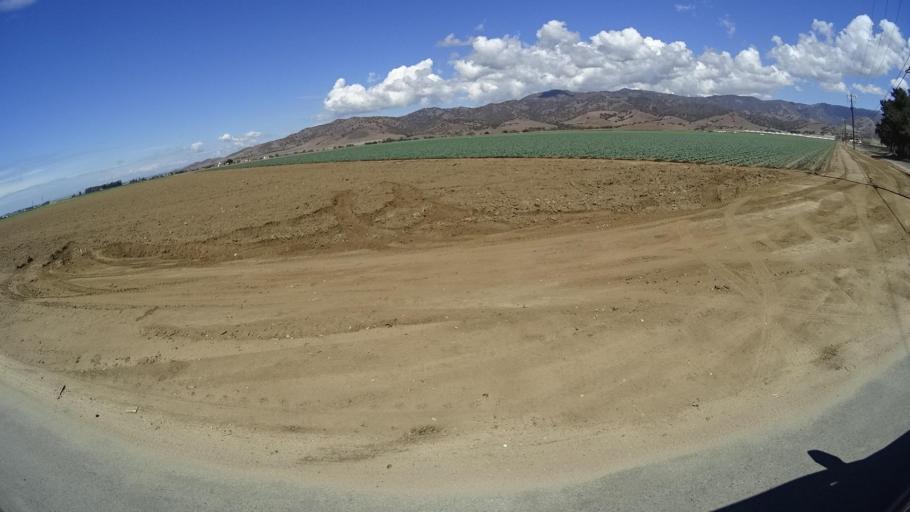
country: US
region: California
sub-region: Monterey County
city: Chualar
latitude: 36.6191
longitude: -121.5103
